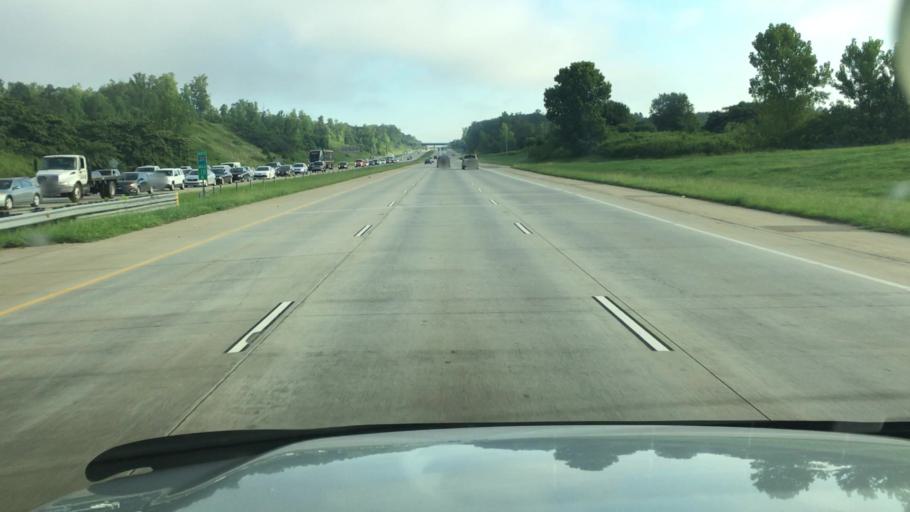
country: US
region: North Carolina
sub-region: Gaston County
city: Mount Holly
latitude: 35.2515
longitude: -80.9684
